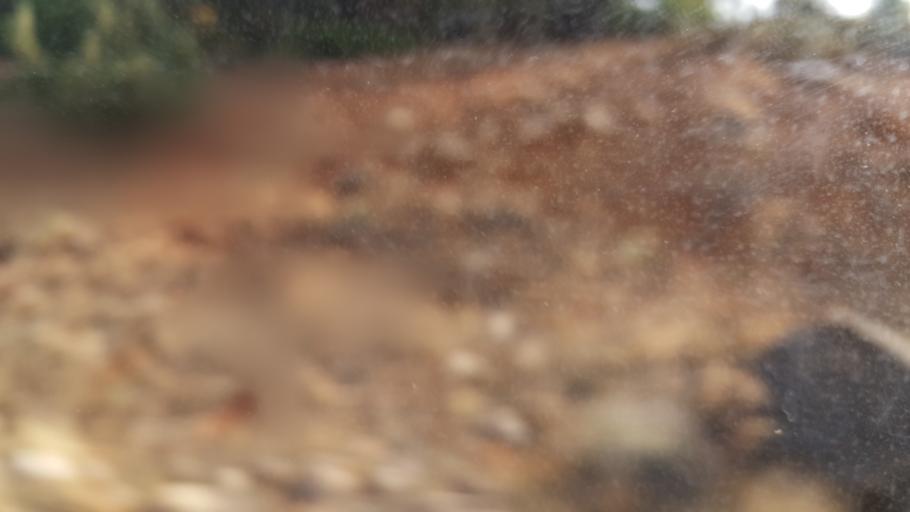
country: TR
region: Eskisehir
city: Mihaliccik
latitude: 39.9642
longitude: 31.3873
